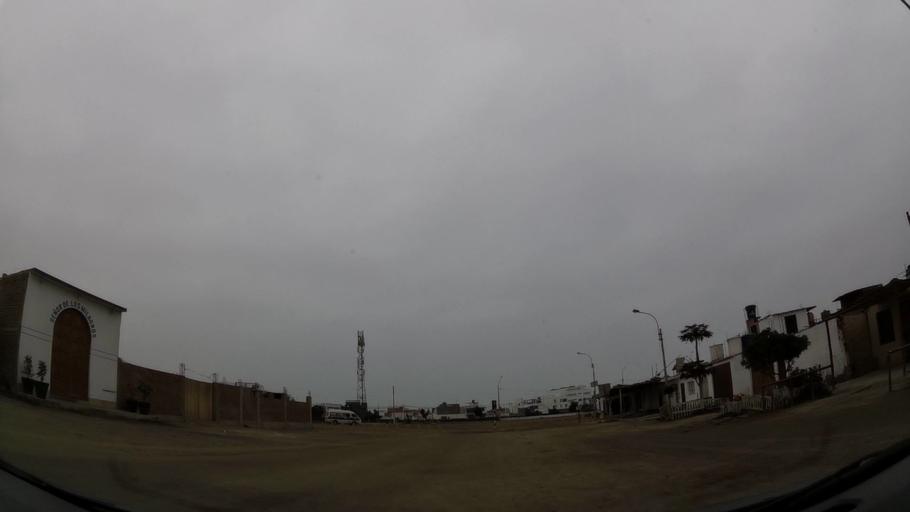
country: PE
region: Lima
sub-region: Lima
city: Punta Hermosa
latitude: -12.3349
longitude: -76.8231
